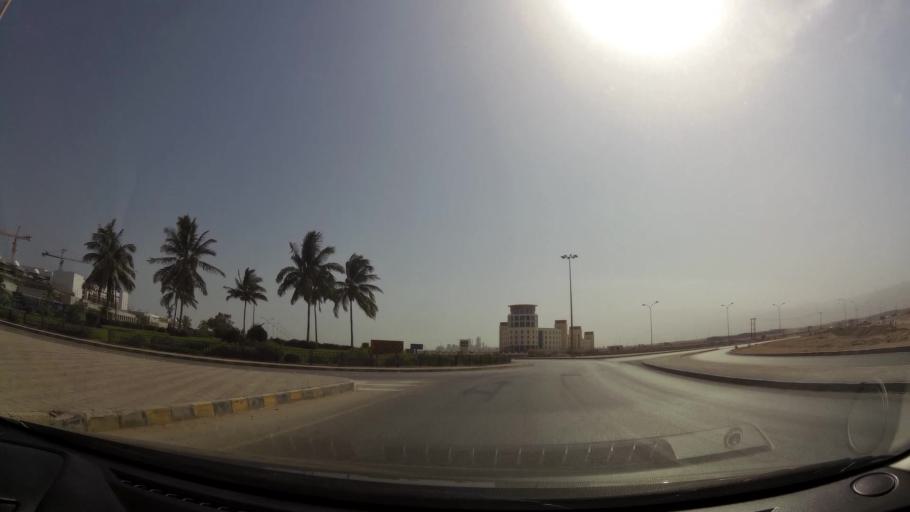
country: OM
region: Zufar
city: Salalah
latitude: 16.9852
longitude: 54.0177
